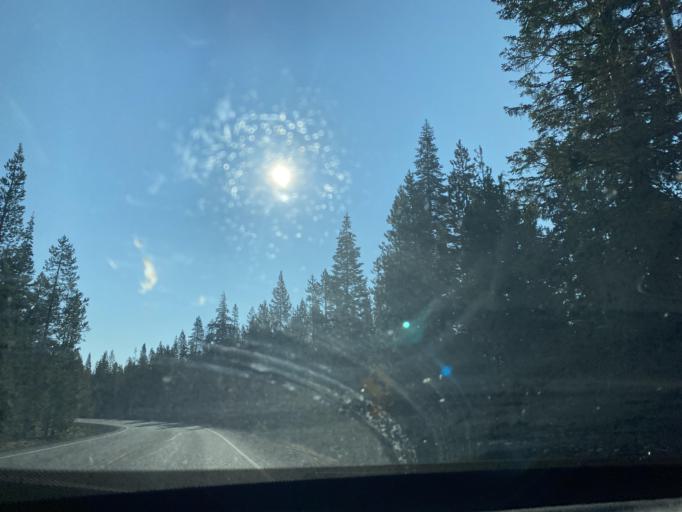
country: US
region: Oregon
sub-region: Deschutes County
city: Three Rivers
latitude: 43.7069
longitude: -121.2869
